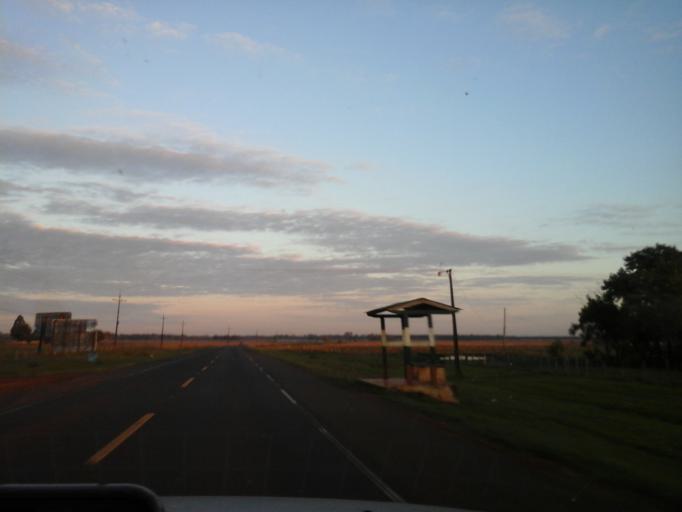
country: PY
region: Itapua
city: General Delgado
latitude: -27.0837
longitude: -56.5543
